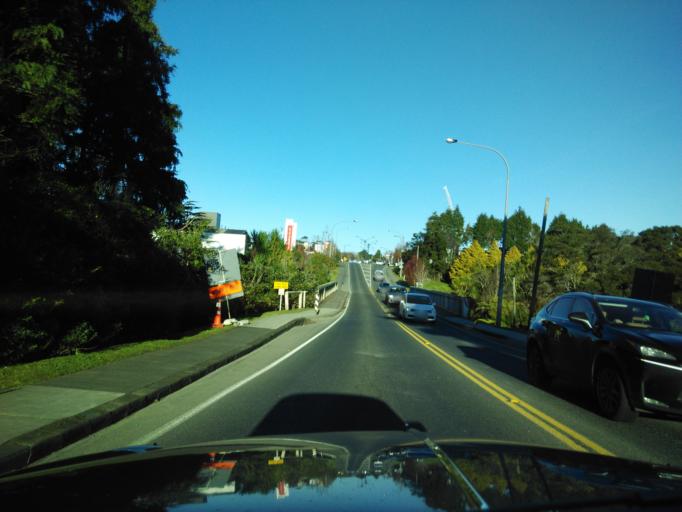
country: NZ
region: Auckland
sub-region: Auckland
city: Rothesay Bay
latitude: -36.7228
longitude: 174.6924
